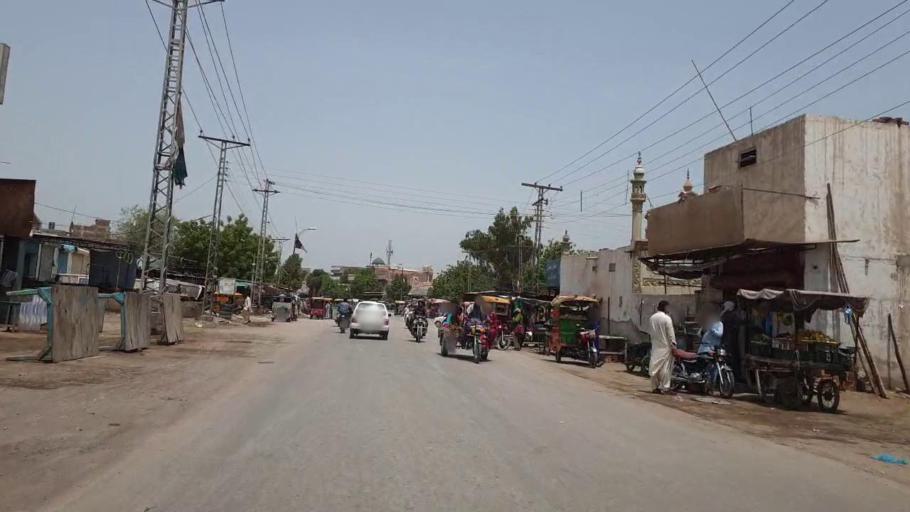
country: PK
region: Sindh
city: Nawabshah
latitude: 26.2515
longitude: 68.4256
